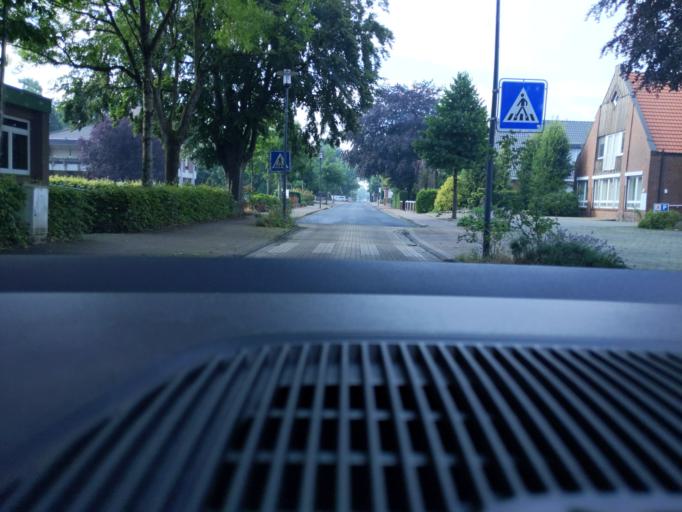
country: NL
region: Drenthe
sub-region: Gemeente Emmen
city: Emmer-Compascuum
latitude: 52.8367
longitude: 7.1013
